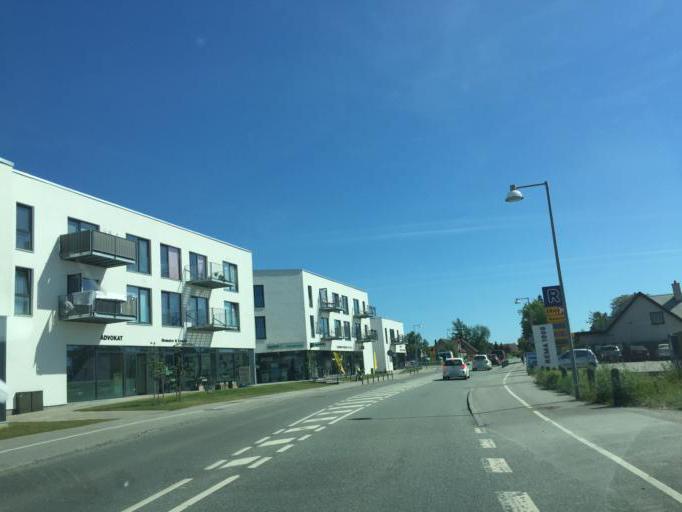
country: DK
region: Zealand
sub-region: Stevns Kommune
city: Stroby Egede
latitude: 55.4172
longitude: 12.2430
